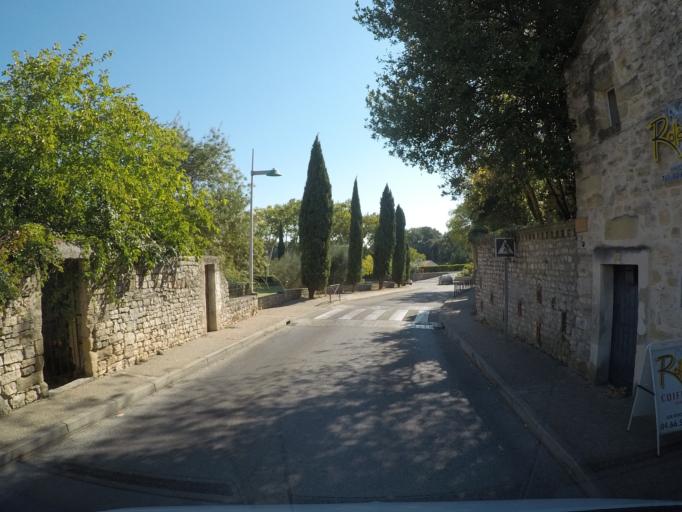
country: FR
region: Languedoc-Roussillon
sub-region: Departement du Gard
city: Montaren-et-Saint-Mediers
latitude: 44.0006
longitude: 4.3739
